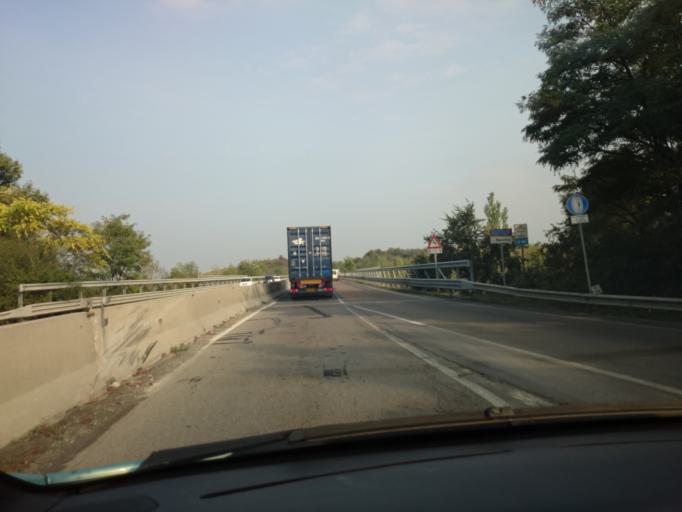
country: IT
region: Emilia-Romagna
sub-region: Provincia di Reggio Emilia
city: Veggia-Villalunga
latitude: 44.5597
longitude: 10.7697
